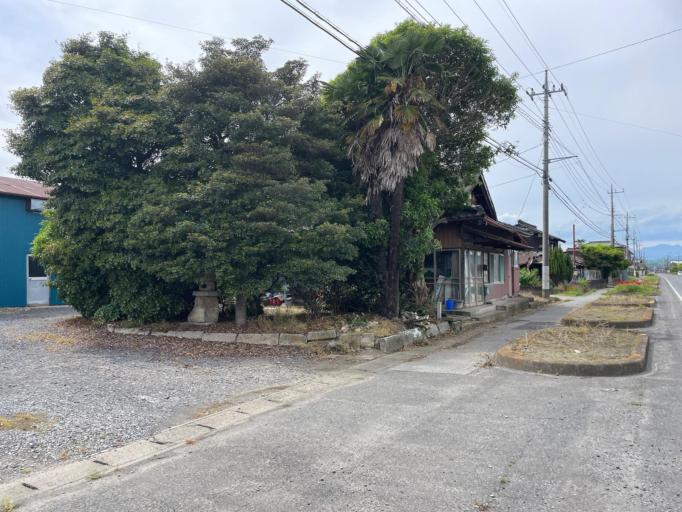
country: JP
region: Tochigi
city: Mibu
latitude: 36.4641
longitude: 139.7685
